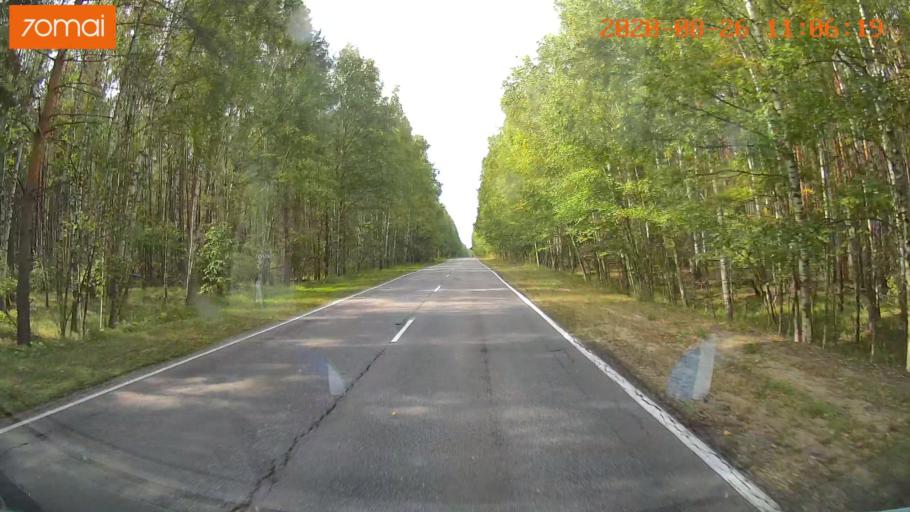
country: RU
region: Rjazan
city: Izhevskoye
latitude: 54.5230
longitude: 41.1510
